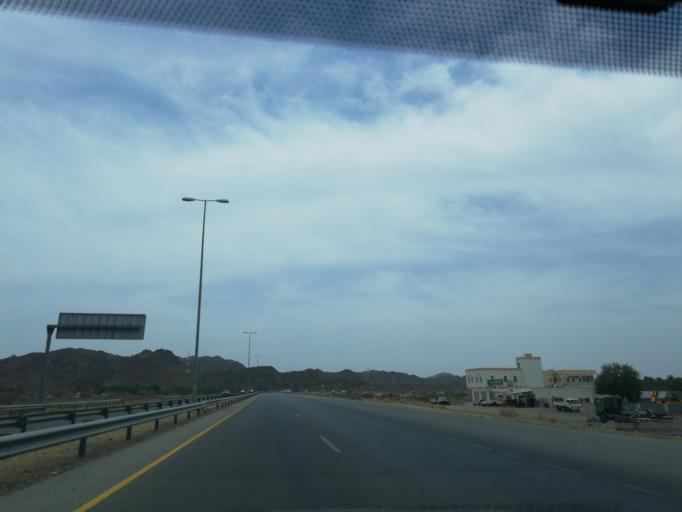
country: OM
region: Muhafazat ad Dakhiliyah
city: Izki
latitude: 22.9904
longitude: 57.7915
